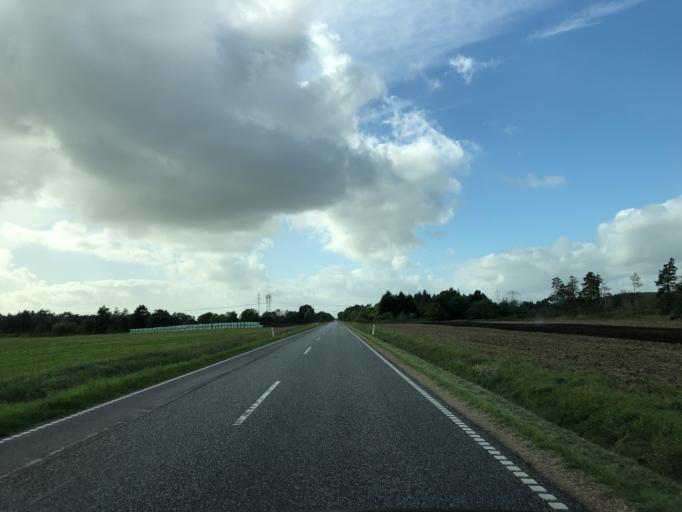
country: DK
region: Central Jutland
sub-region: Holstebro Kommune
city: Holstebro
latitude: 56.3700
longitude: 8.5558
